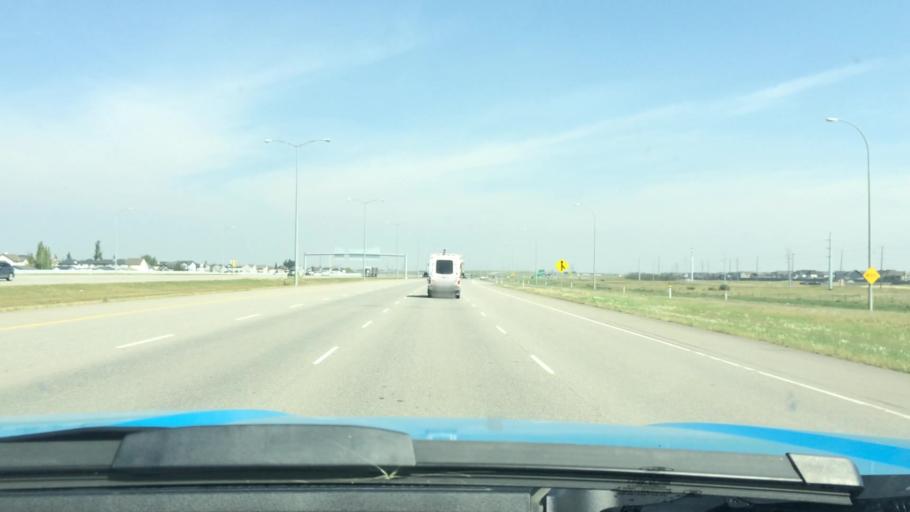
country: CA
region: Alberta
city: Chestermere
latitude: 50.9057
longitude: -113.9421
